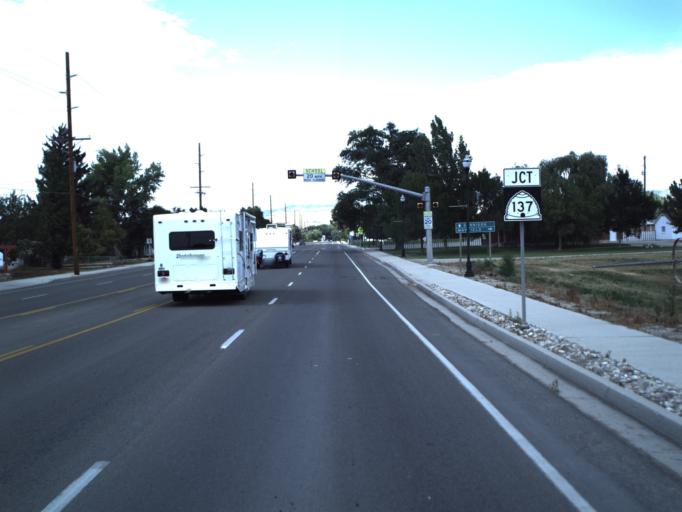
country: US
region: Utah
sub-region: Sanpete County
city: Gunnison
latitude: 39.1406
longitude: -111.8188
